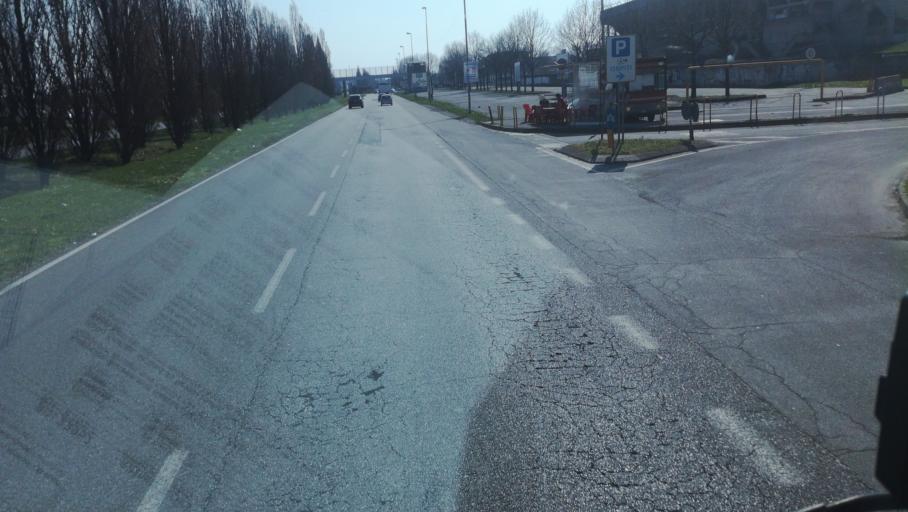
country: IT
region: Lombardy
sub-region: Provincia di Monza e Brianza
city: Villasanta
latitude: 45.5845
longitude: 9.3101
